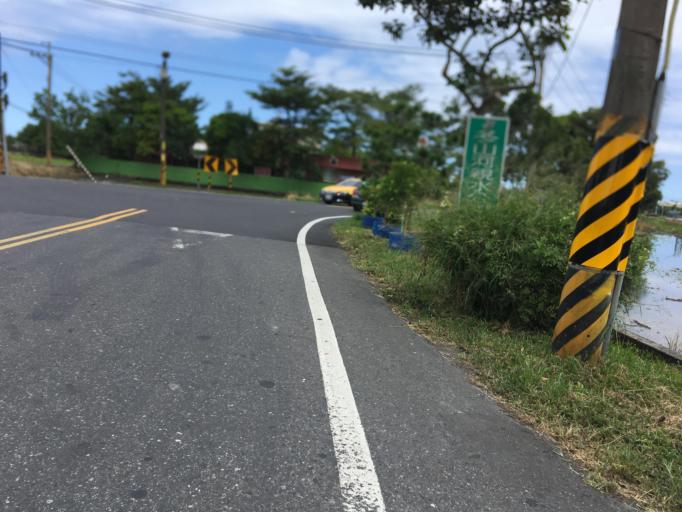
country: TW
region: Taiwan
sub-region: Yilan
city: Yilan
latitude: 24.6837
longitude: 121.8080
